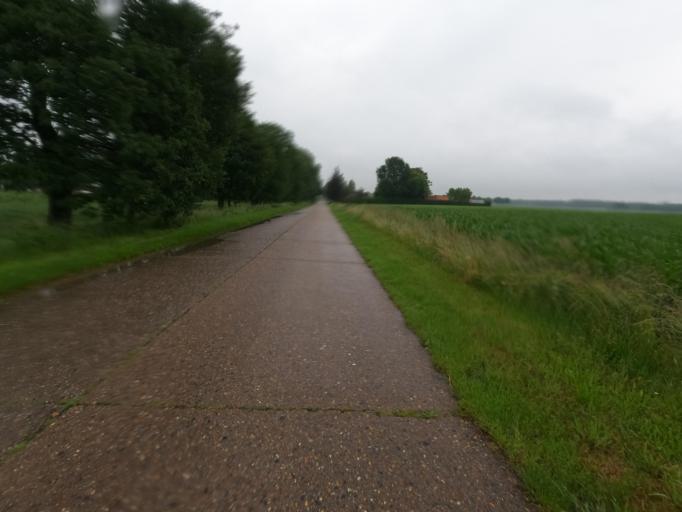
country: BE
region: Flanders
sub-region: Provincie Antwerpen
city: Kalmthout
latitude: 51.3902
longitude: 4.5181
